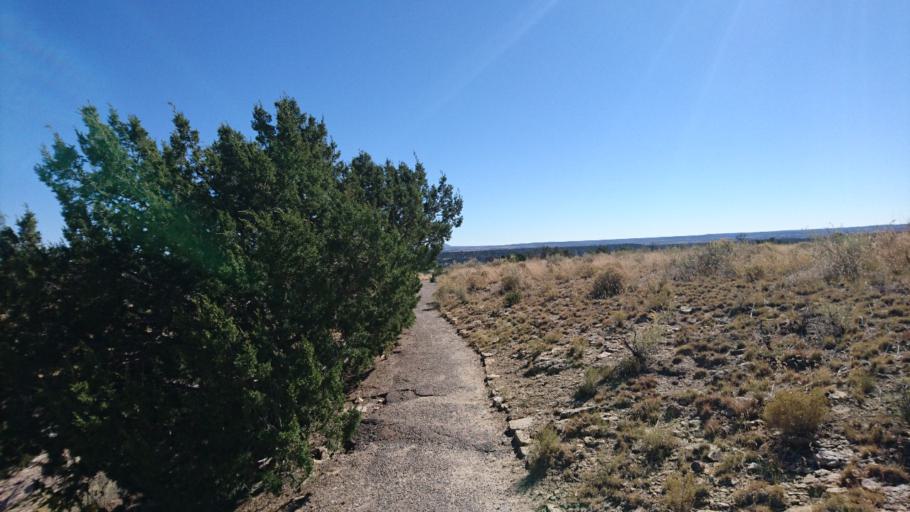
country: US
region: New Mexico
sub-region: McKinley County
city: Thoreau
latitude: 35.0377
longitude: -108.3532
